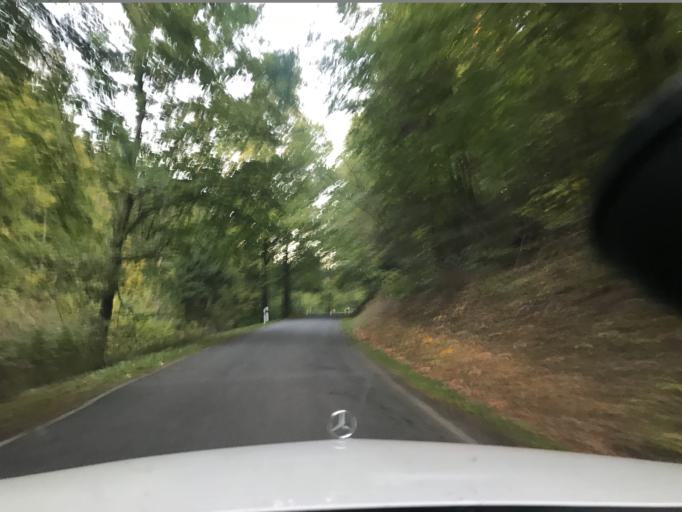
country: DE
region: Thuringia
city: Heyerode
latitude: 51.1987
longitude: 10.3010
